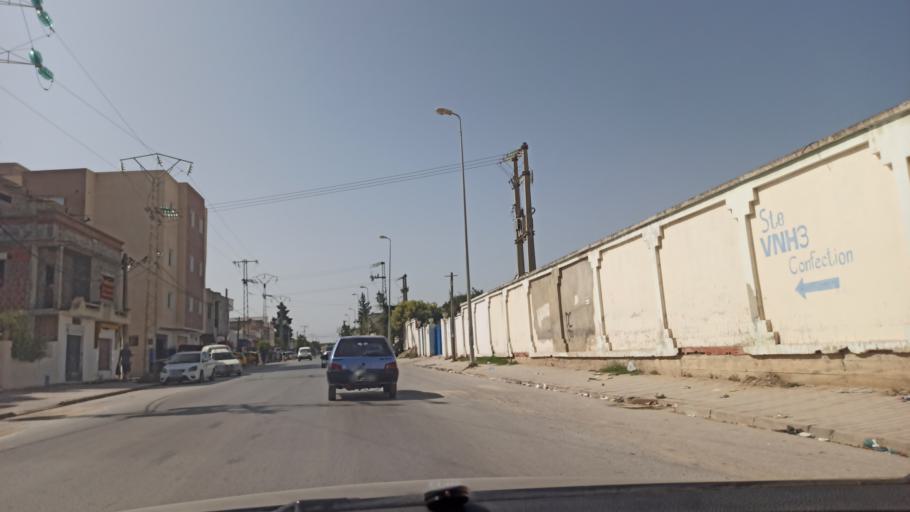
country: TN
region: Manouba
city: Manouba
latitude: 36.7618
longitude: 10.1082
